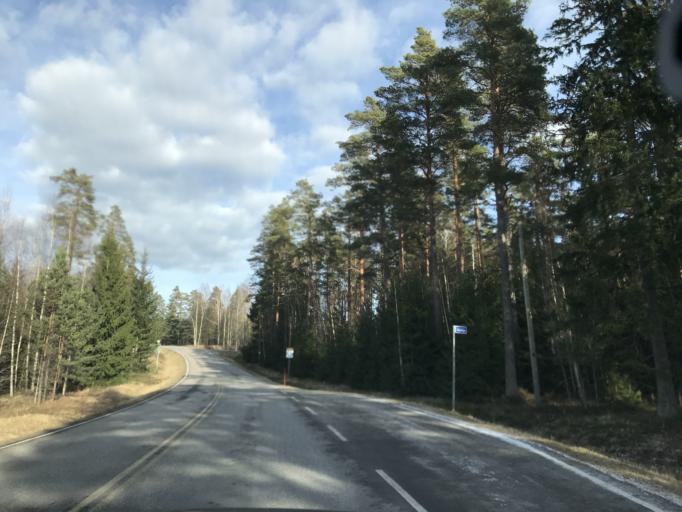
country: FI
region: Uusimaa
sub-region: Raaseporin
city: Ekenaes
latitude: 60.0673
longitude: 23.2808
